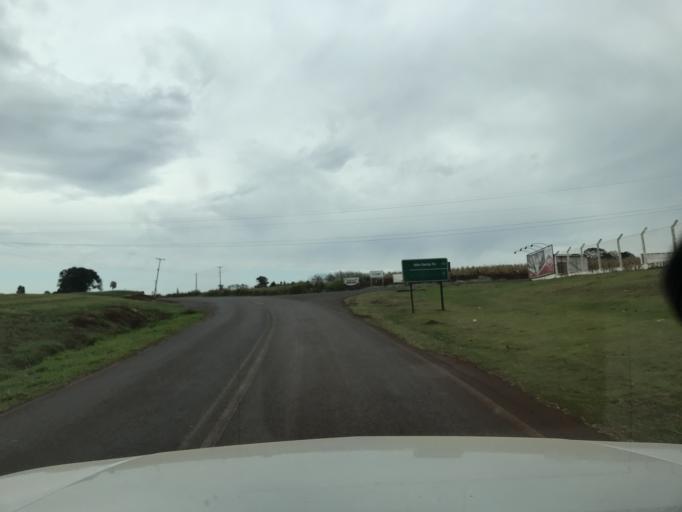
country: BR
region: Parana
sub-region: Marechal Candido Rondon
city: Marechal Candido Rondon
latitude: -24.4553
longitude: -53.9393
